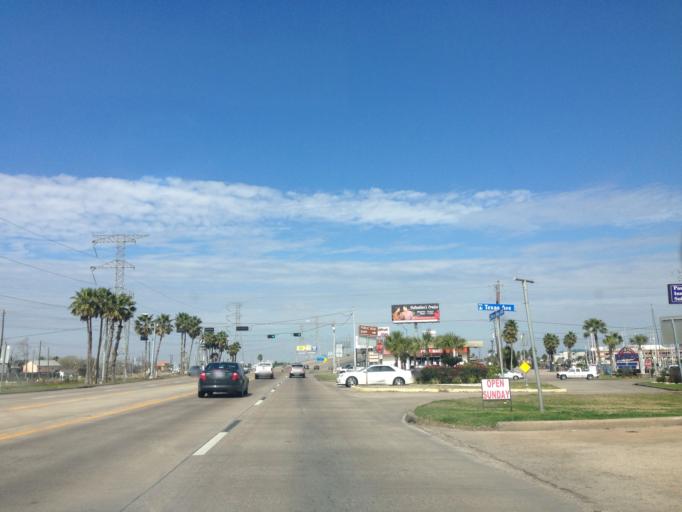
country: US
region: Texas
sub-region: Galveston County
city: Kemah
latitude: 29.5424
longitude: -95.0206
